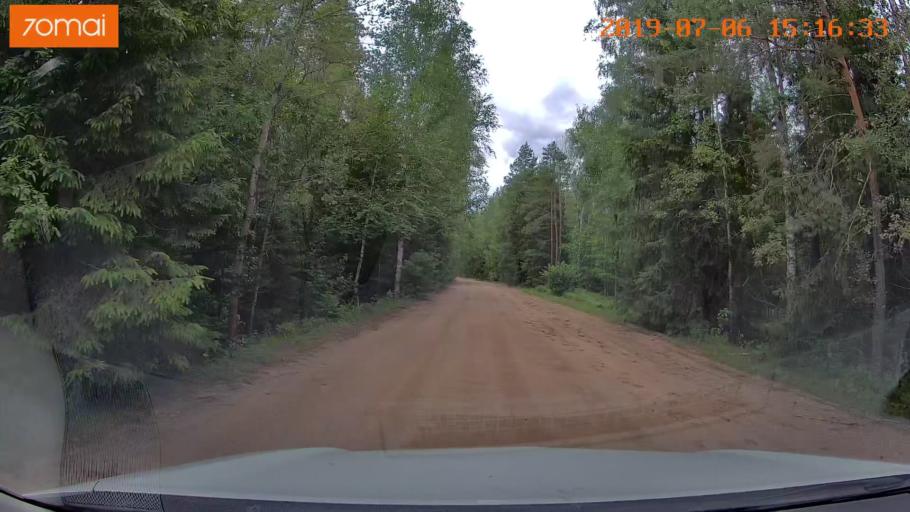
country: BY
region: Minsk
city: Ivyanyets
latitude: 53.9819
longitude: 26.6771
